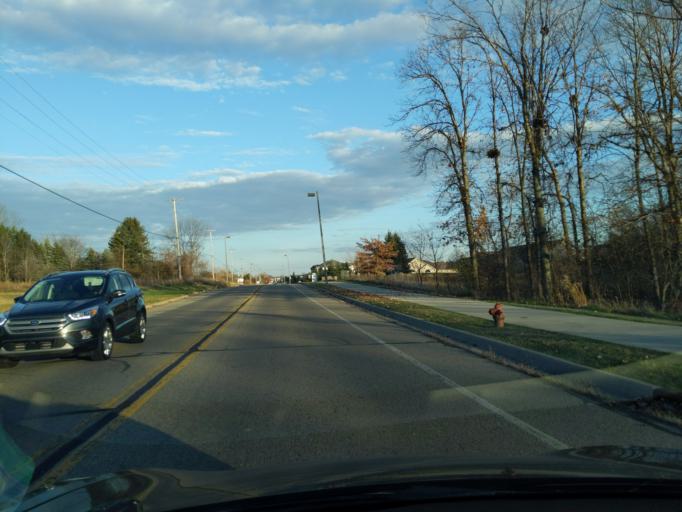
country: US
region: Michigan
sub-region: Ingham County
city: East Lansing
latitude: 42.7731
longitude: -84.5019
